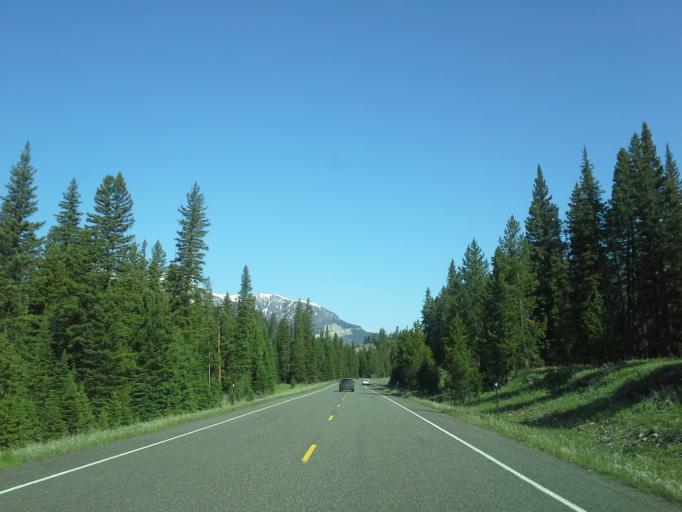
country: US
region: Montana
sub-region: Carbon County
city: Red Lodge
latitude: 44.9512
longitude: -109.7942
